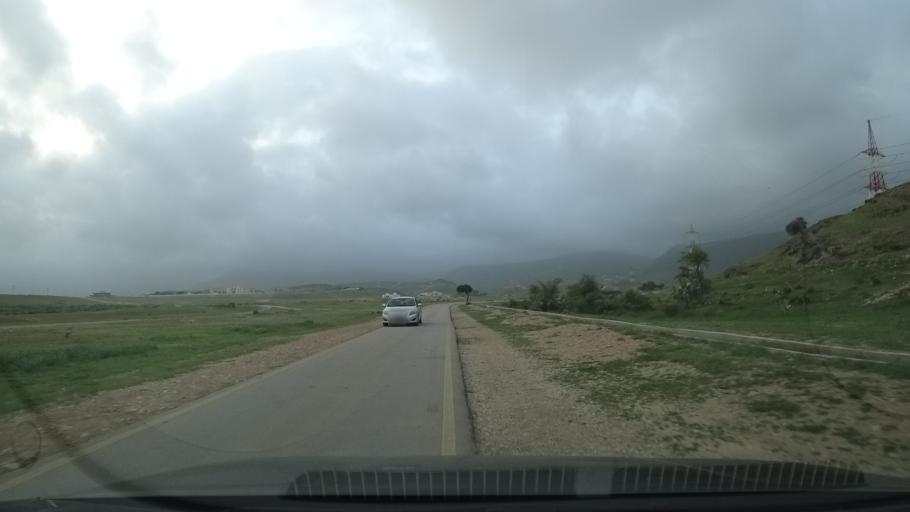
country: OM
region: Zufar
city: Salalah
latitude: 17.1122
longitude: 54.2272
